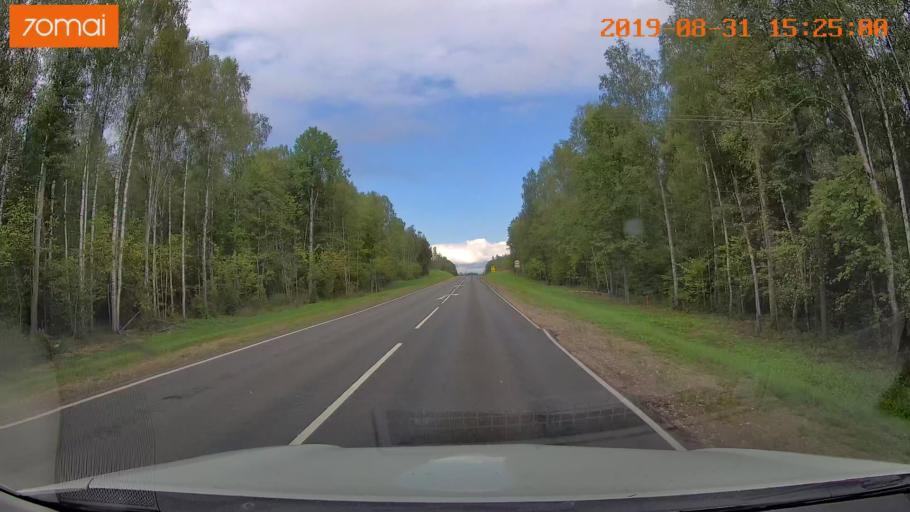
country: RU
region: Kaluga
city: Baryatino
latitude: 54.5354
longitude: 34.5131
